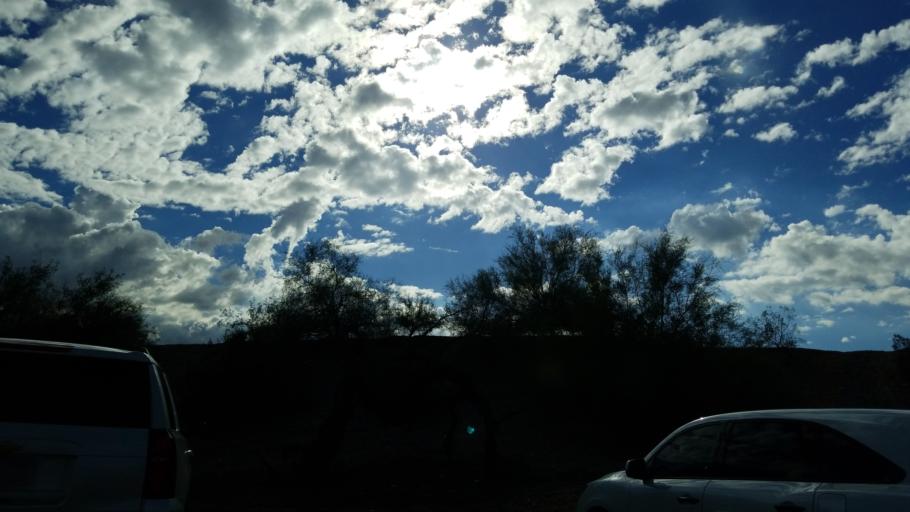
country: US
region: Arizona
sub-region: Mohave County
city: Lake Havasu City
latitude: 34.4664
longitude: -114.3487
